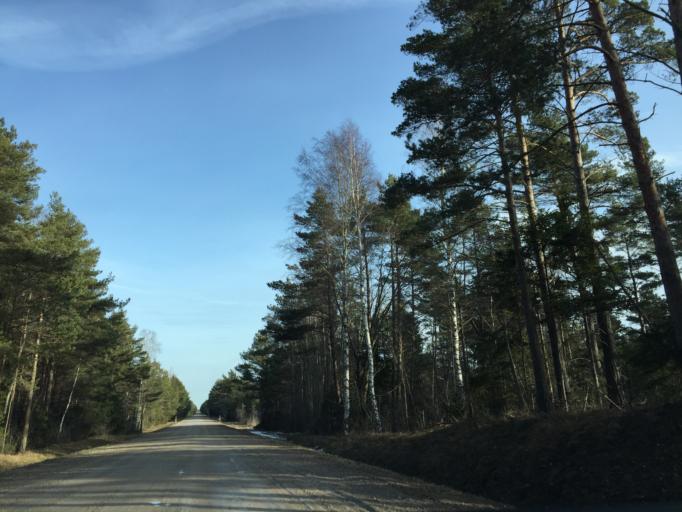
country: EE
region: Saare
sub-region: Kuressaare linn
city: Kuressaare
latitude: 58.3051
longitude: 21.9668
